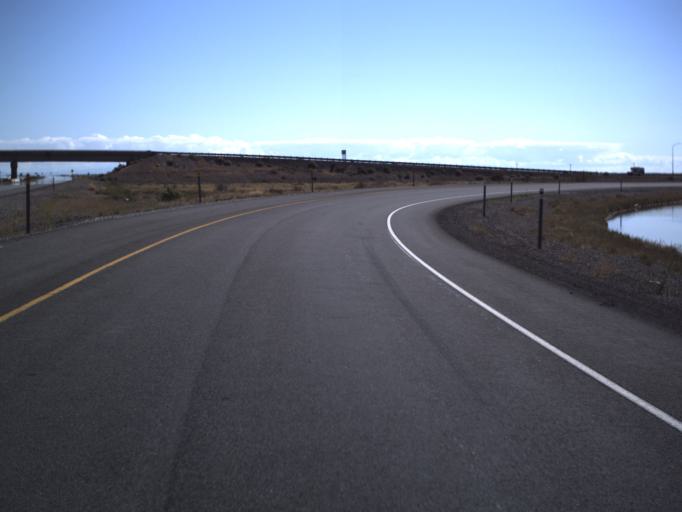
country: US
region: Utah
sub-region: Tooele County
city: Wendover
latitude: 40.7424
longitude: -113.9748
